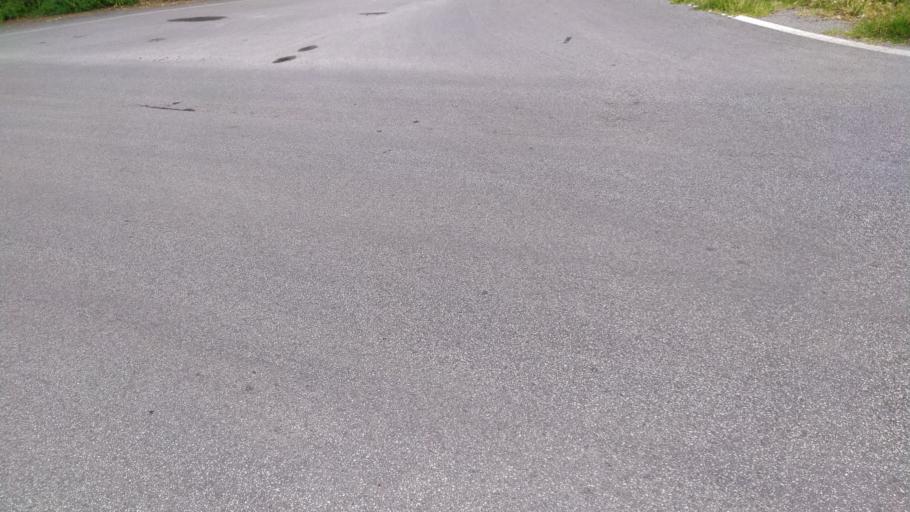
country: IT
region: Sicily
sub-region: Messina
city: San Filippo del Mela
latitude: 38.1689
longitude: 15.2820
